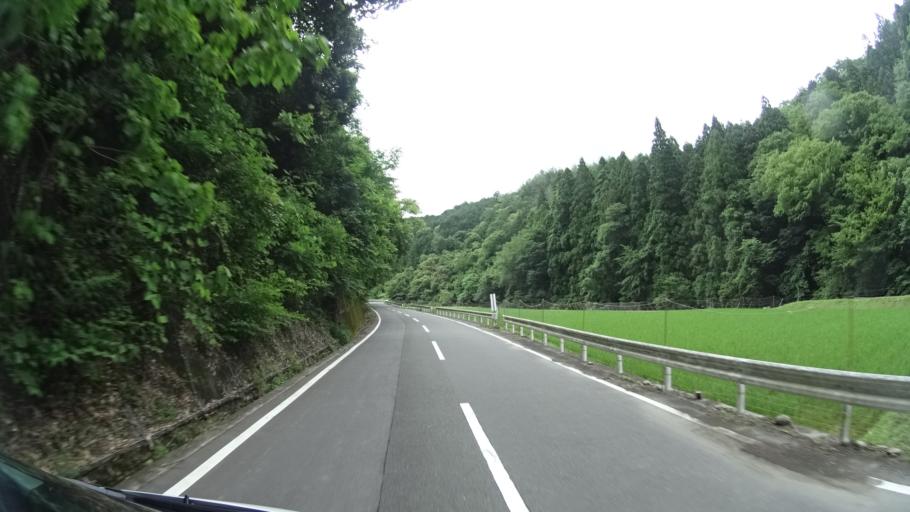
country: JP
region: Hyogo
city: Sasayama
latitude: 35.0640
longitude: 135.3982
